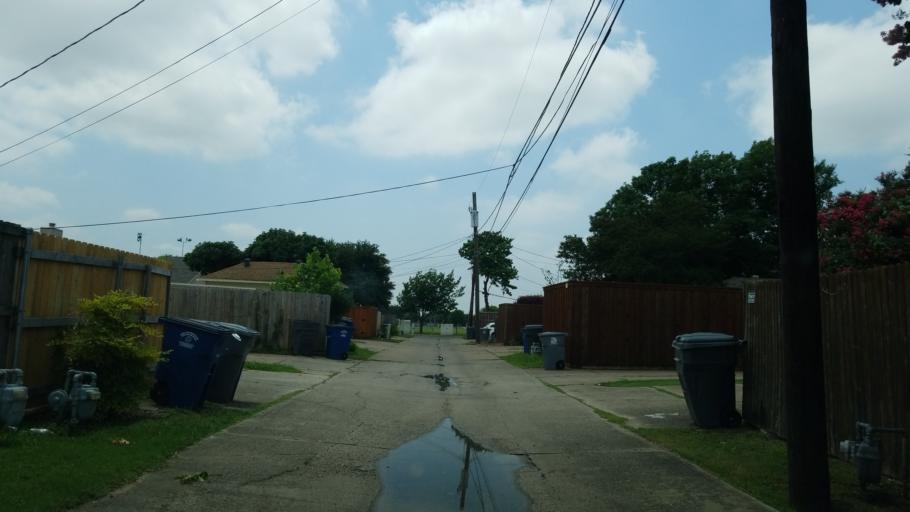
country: US
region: Texas
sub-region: Dallas County
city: Farmers Branch
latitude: 32.9054
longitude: -96.8760
